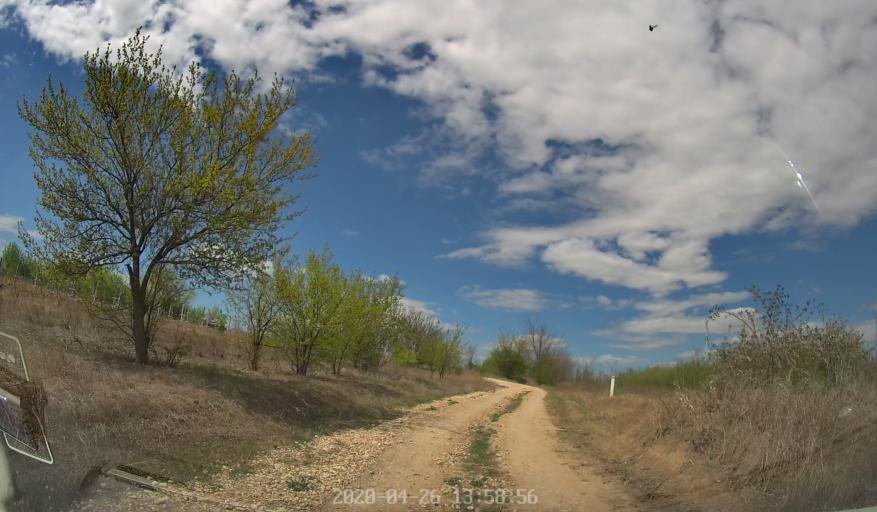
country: MD
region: Telenesti
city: Cocieri
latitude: 47.2689
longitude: 29.1196
